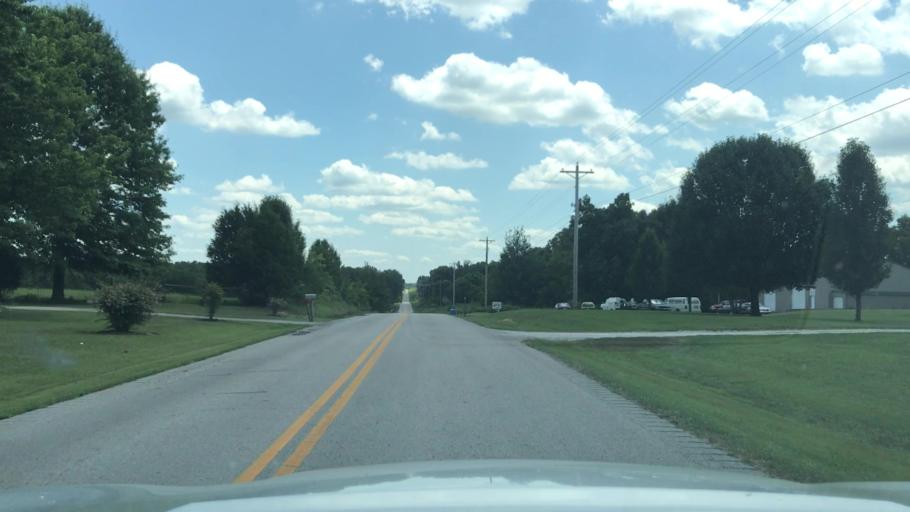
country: US
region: Kentucky
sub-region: Christian County
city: Hopkinsville
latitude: 37.0020
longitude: -87.3678
